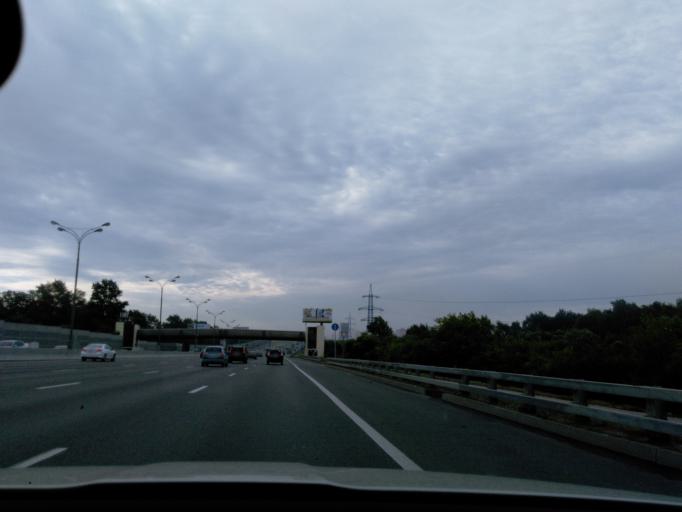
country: RU
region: Moscow
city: Yaroslavskiy
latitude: 55.8913
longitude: 37.7074
